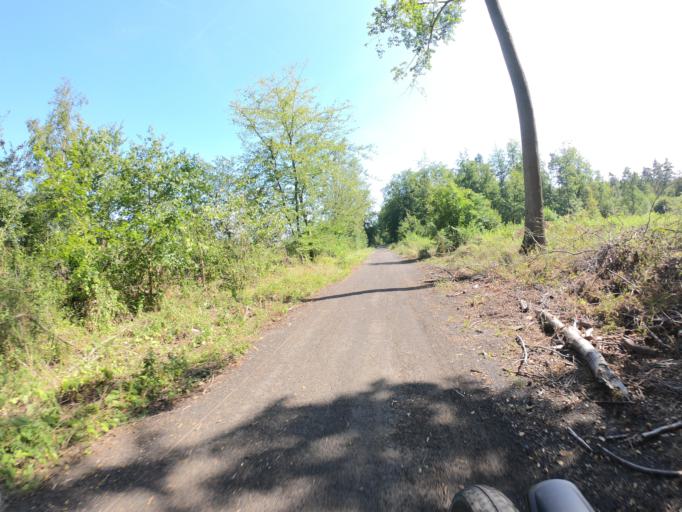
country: DE
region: Hesse
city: Morfelden-Walldorf
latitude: 49.9985
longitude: 8.6114
